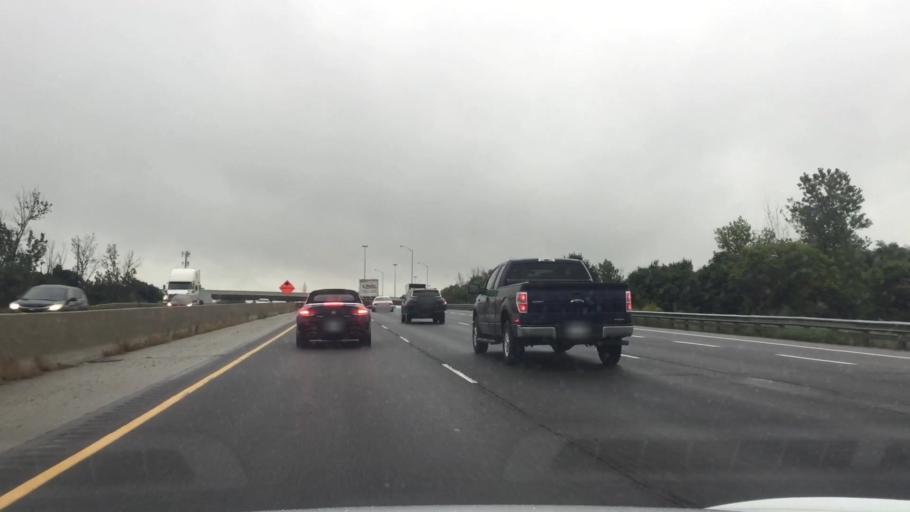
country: CA
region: Ontario
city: Cambridge
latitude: 43.4009
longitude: -80.3807
